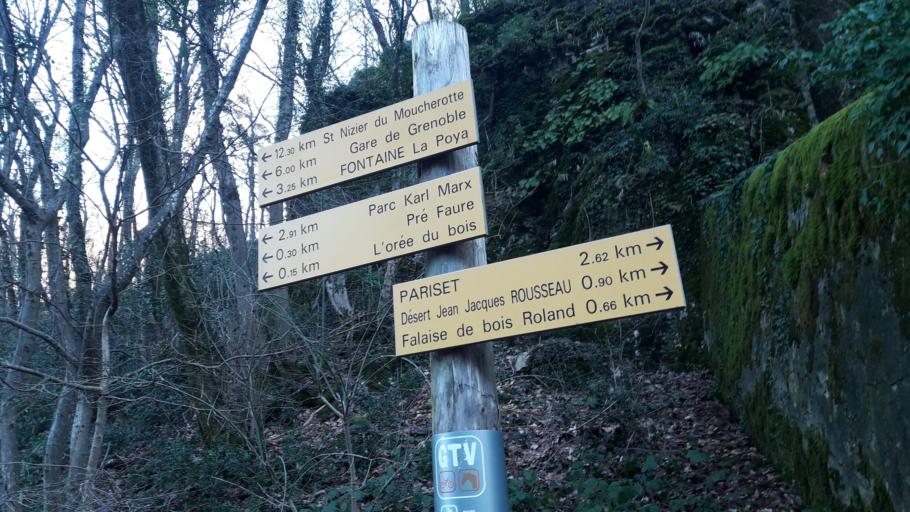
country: FR
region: Rhone-Alpes
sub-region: Departement de l'Isere
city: Fontaine
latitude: 45.1795
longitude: 5.6705
